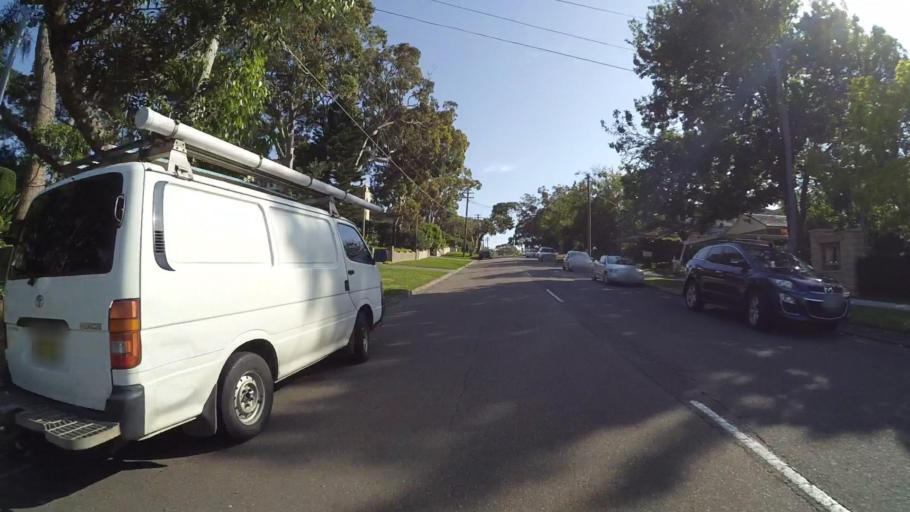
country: AU
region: New South Wales
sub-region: Sutherland Shire
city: Cronulla
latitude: -34.0628
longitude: 151.1381
